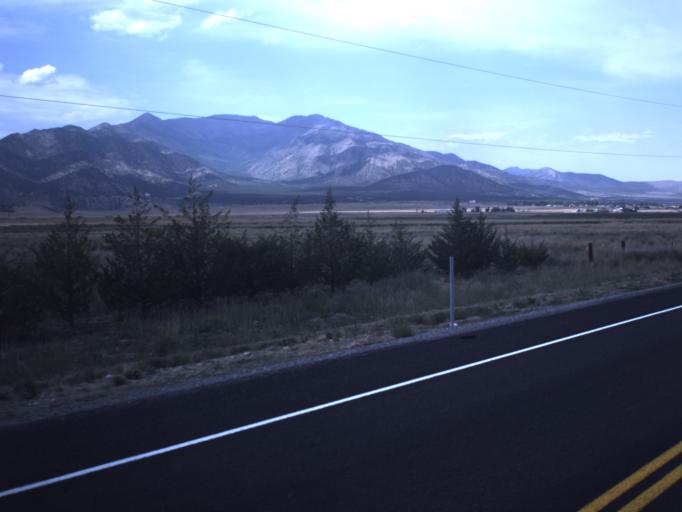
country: US
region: Utah
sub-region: Utah County
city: Eagle Mountain
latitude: 40.2668
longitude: -112.0936
